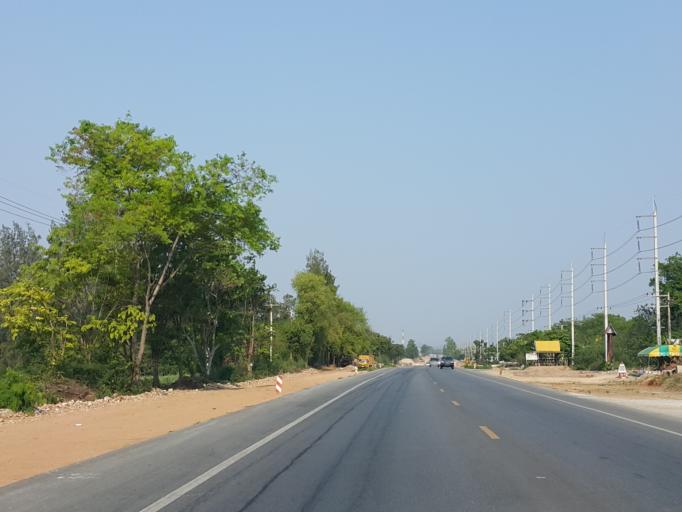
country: TH
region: Kanchanaburi
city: Sai Yok
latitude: 14.0872
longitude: 99.3395
